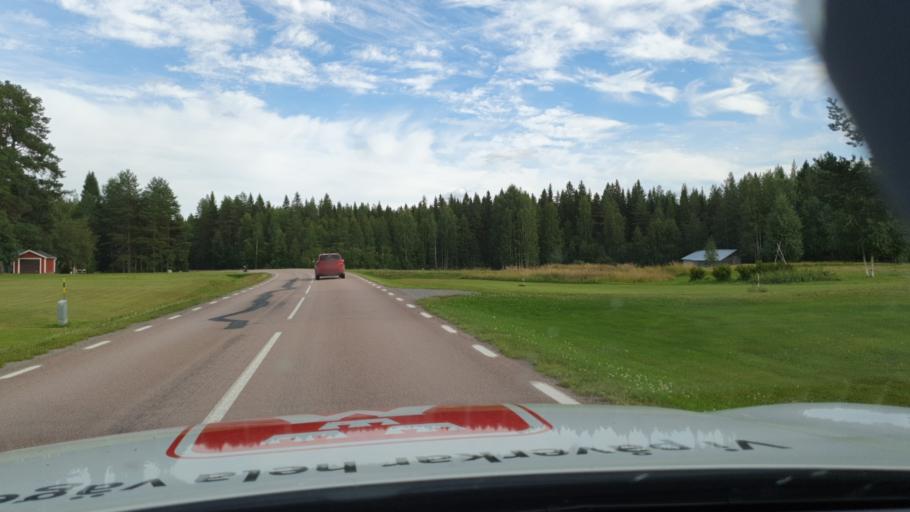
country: SE
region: Jaemtland
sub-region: Stroemsunds Kommun
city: Stroemsund
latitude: 63.6580
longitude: 15.9707
